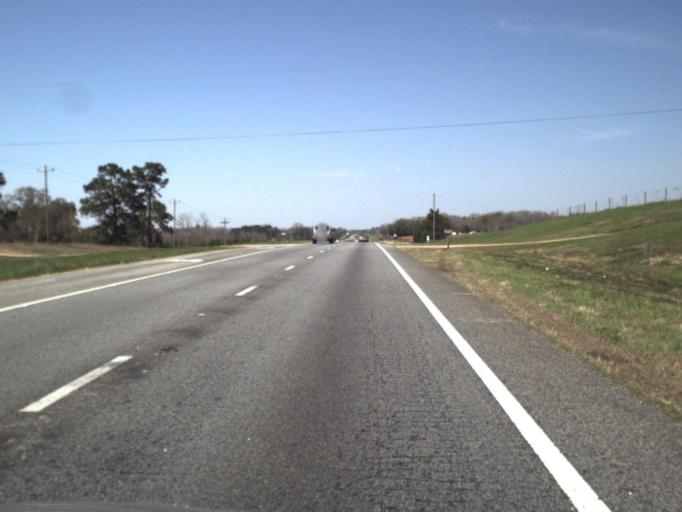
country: US
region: Florida
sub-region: Jackson County
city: Graceville
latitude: 30.9086
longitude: -85.3772
